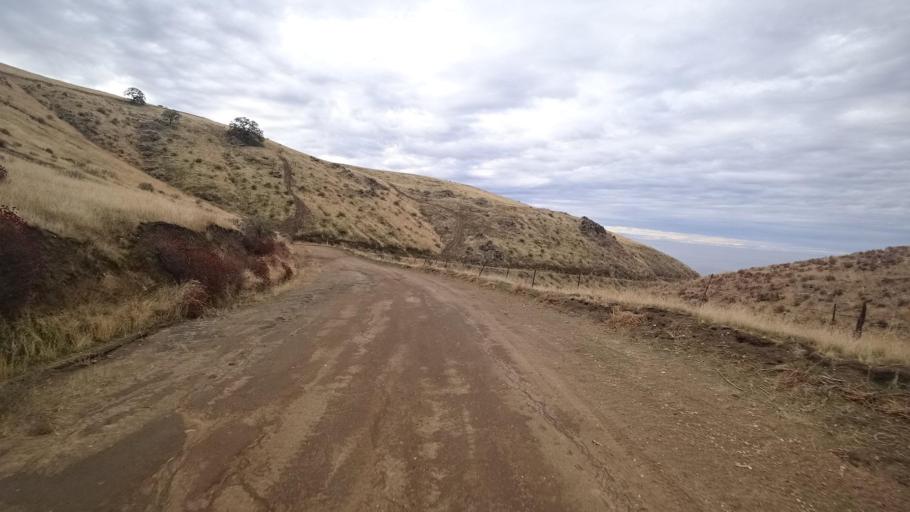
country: US
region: California
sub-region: Kern County
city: Arvin
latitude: 35.1326
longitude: -118.7683
